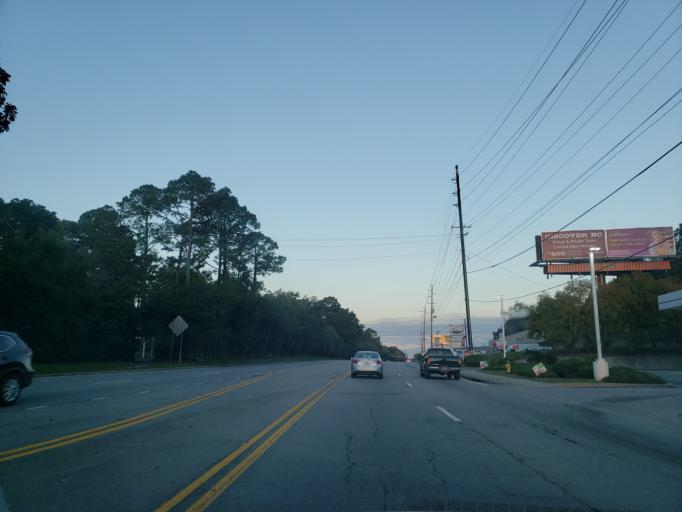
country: US
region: Georgia
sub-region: Chatham County
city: Thunderbolt
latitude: 32.0231
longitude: -81.0898
